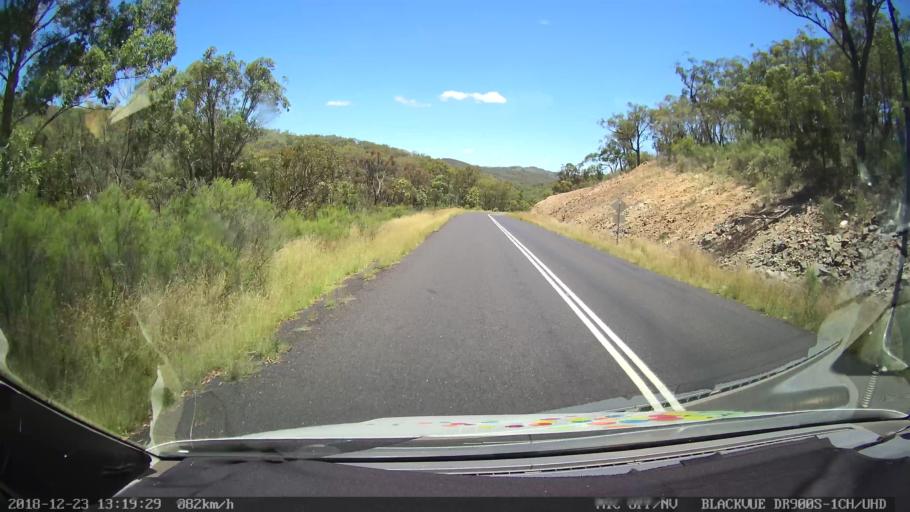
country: AU
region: New South Wales
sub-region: Armidale Dumaresq
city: Armidale
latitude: -30.4828
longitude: 151.4630
